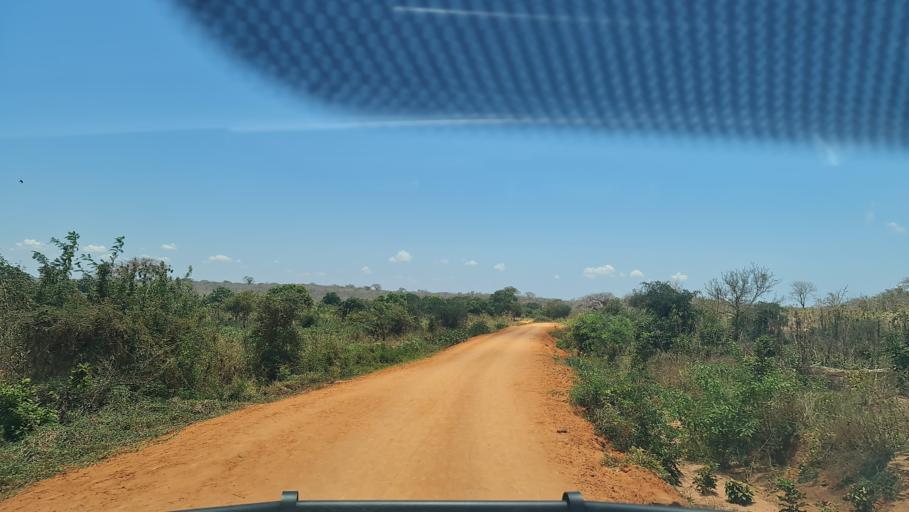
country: MZ
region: Nampula
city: Nacala
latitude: -14.2132
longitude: 40.6789
